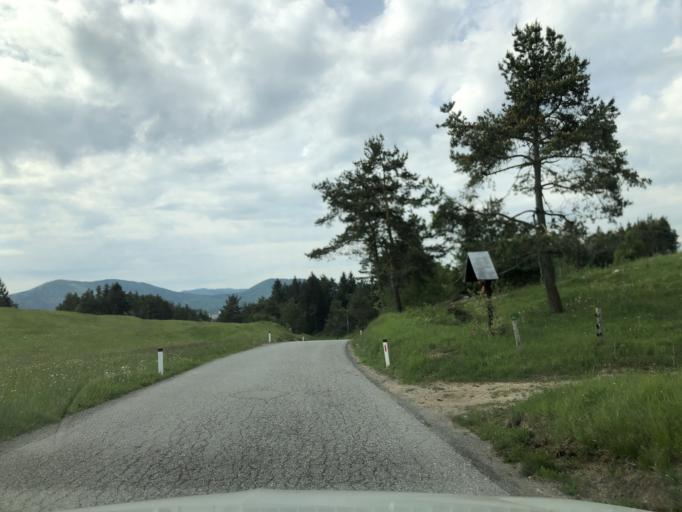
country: SI
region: Bloke
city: Nova Vas
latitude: 45.7830
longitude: 14.5010
